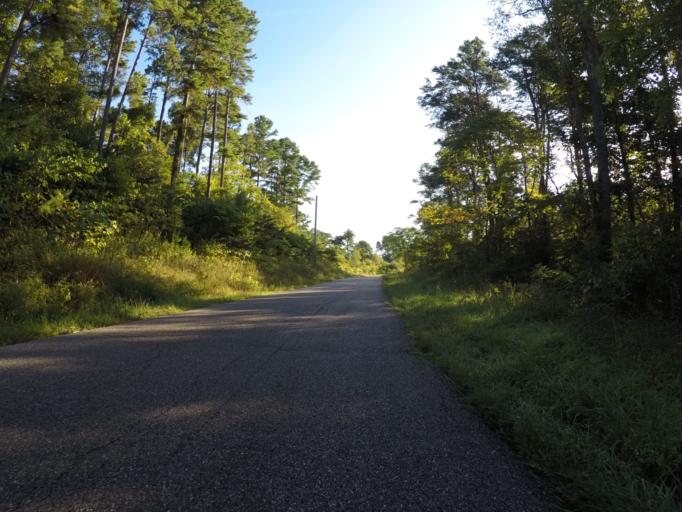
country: US
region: Ohio
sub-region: Lawrence County
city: Coal Grove
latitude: 38.6044
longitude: -82.5605
